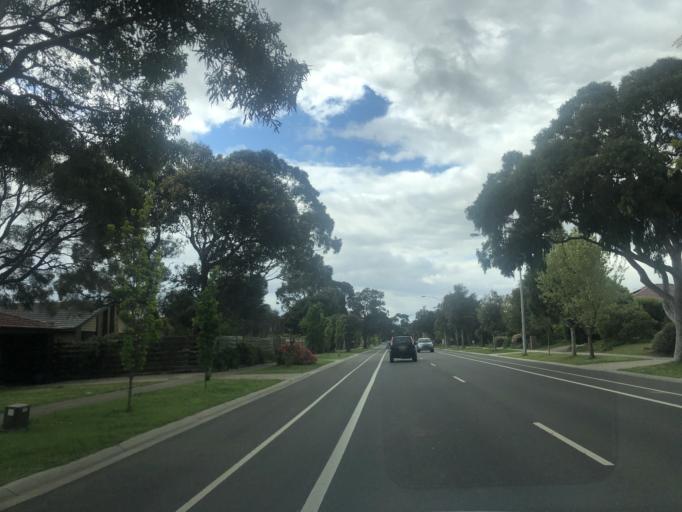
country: AU
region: Victoria
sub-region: Casey
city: Endeavour Hills
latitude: -37.9769
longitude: 145.2458
